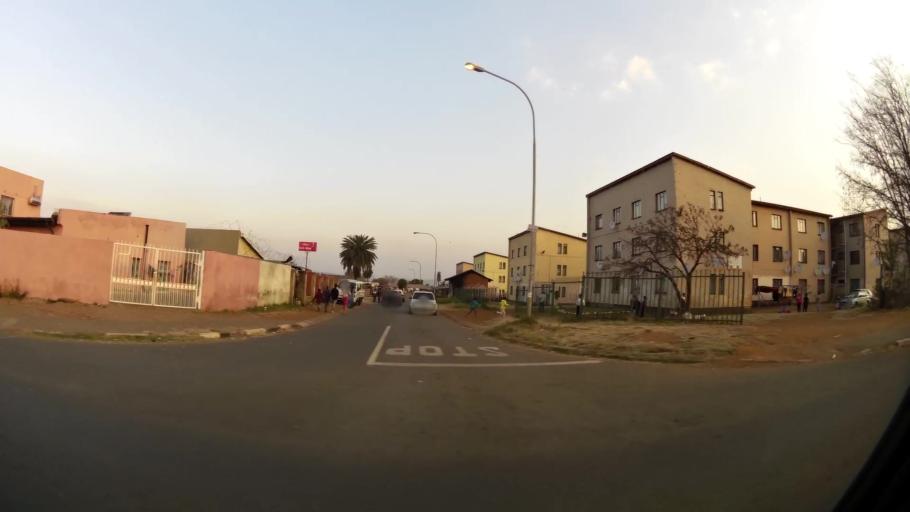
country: ZA
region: Gauteng
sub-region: City of Johannesburg Metropolitan Municipality
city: Soweto
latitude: -26.2919
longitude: 27.8989
